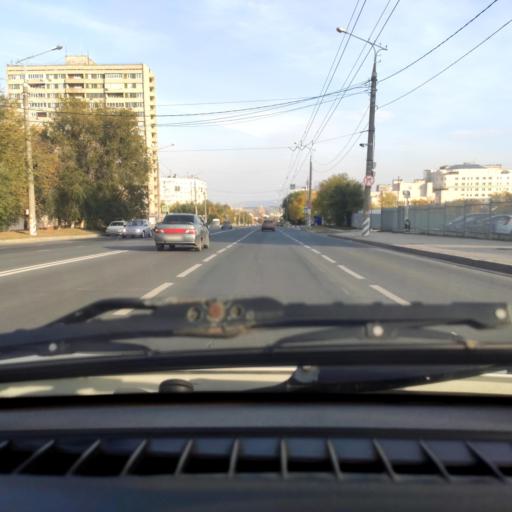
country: RU
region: Samara
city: Zhigulevsk
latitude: 53.4757
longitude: 49.4604
